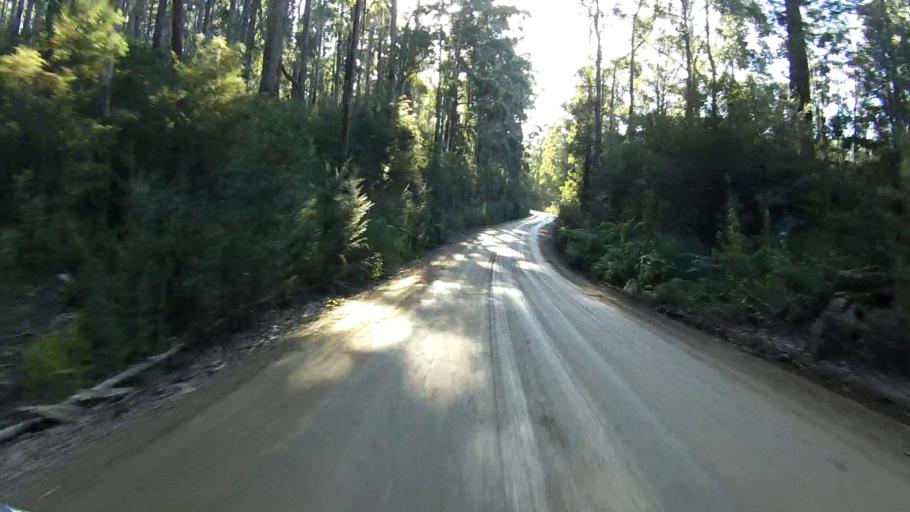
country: AU
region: Tasmania
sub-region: Clarence
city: Sandford
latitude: -43.1228
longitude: 147.9262
